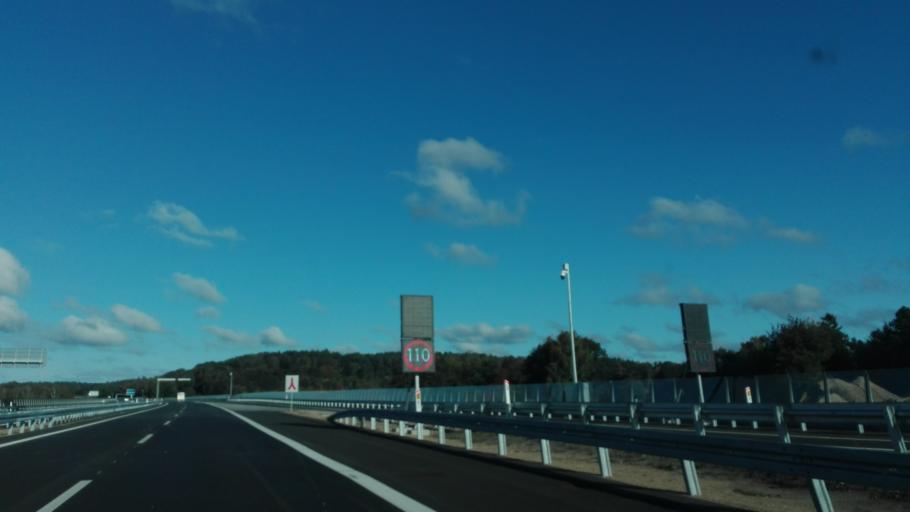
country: DK
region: Central Jutland
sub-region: Silkeborg Kommune
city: Svejbaek
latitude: 56.1708
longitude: 9.6011
